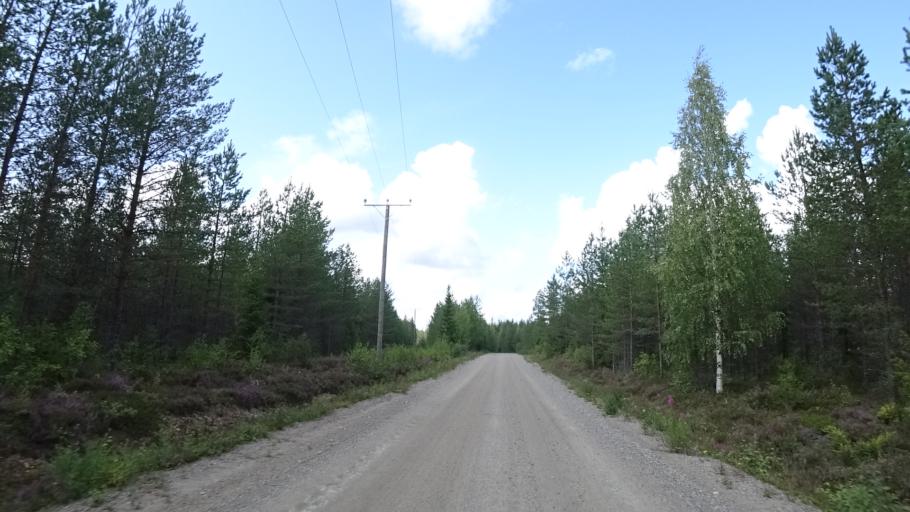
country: FI
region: North Karelia
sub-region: Joensuu
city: Ilomantsi
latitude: 62.9254
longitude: 31.3320
